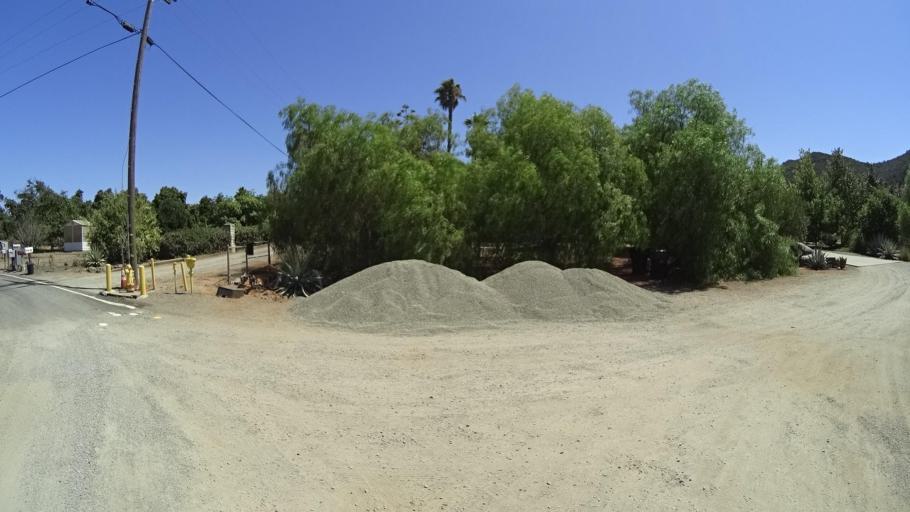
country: US
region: California
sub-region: San Diego County
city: Rainbow
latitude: 33.3765
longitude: -117.1166
